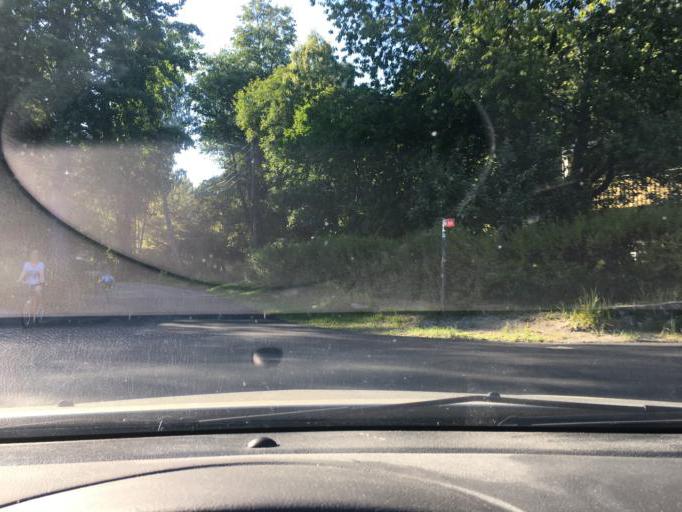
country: SE
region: Stockholm
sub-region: Nacka Kommun
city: Boo
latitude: 59.3260
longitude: 18.2426
